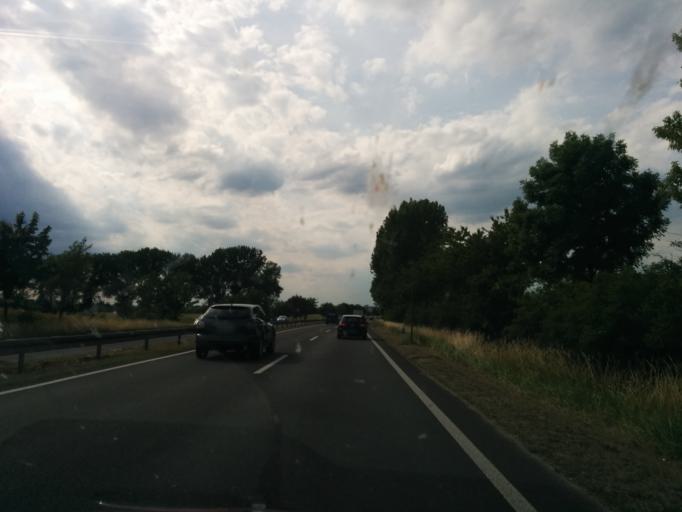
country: DE
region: Thuringia
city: Elxleben
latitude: 51.0381
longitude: 10.9493
